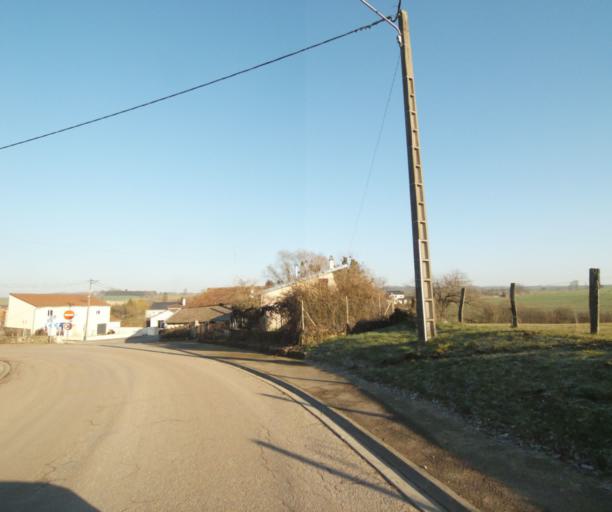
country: FR
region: Champagne-Ardenne
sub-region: Departement de la Haute-Marne
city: Bienville
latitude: 48.5805
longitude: 5.0883
